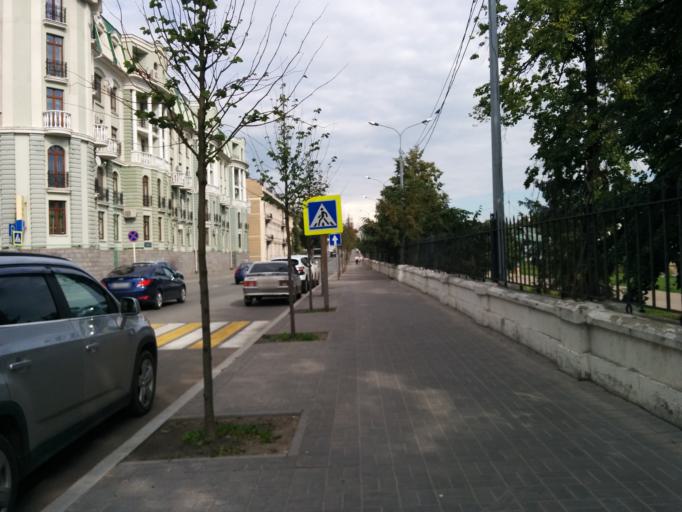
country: RU
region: Tatarstan
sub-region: Gorod Kazan'
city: Kazan
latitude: 55.7958
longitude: 49.1148
